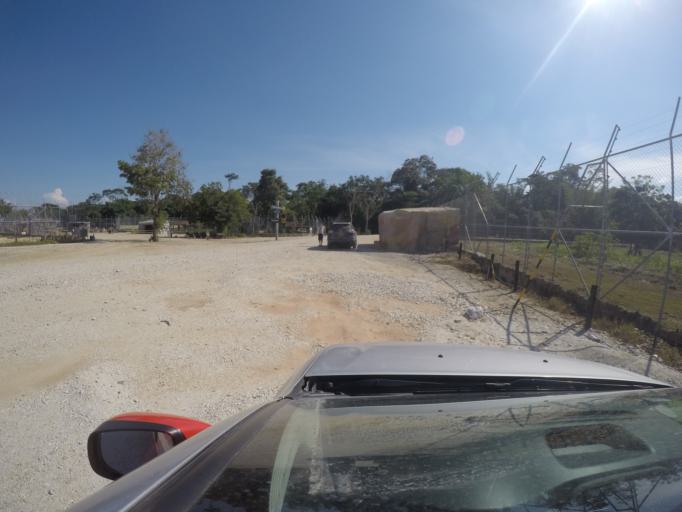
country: CO
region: Antioquia
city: Puerto Triunfo
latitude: 5.9307
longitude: -74.7267
